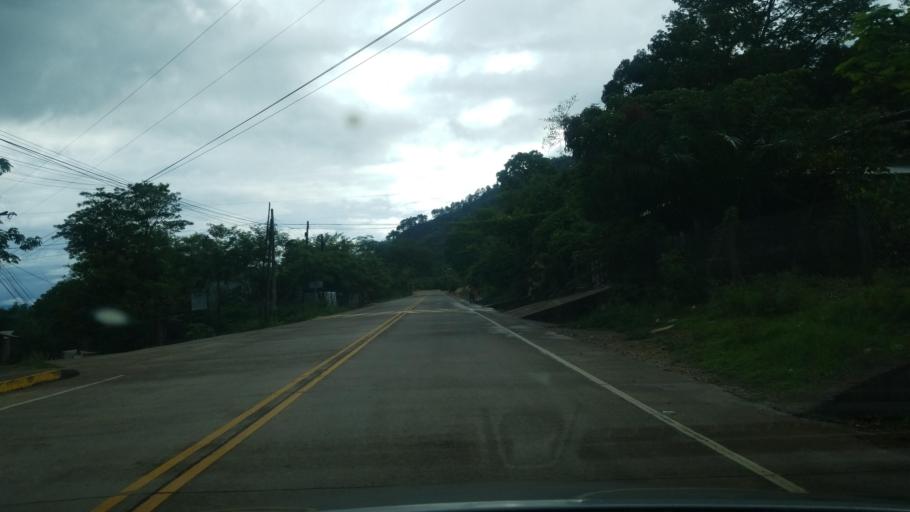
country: HN
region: Copan
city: Copan
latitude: 14.8406
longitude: -89.1759
